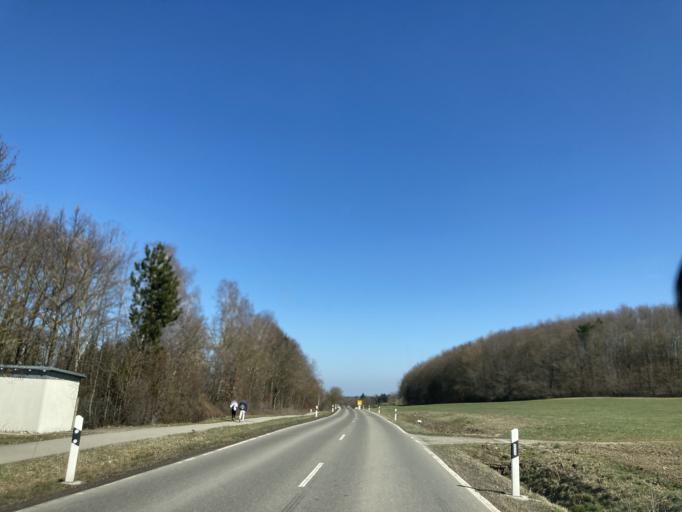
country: DE
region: Baden-Wuerttemberg
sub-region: Tuebingen Region
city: Bodelshausen
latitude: 48.3833
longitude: 8.9631
